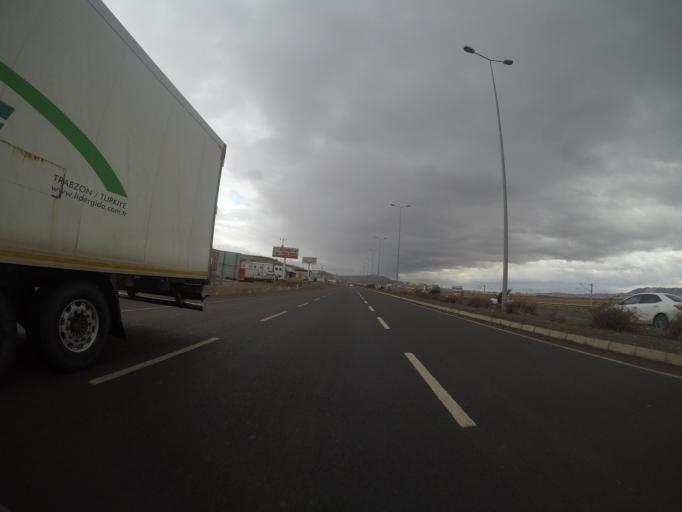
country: TR
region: Kayseri
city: Incesu
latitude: 38.7376
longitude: 35.2916
